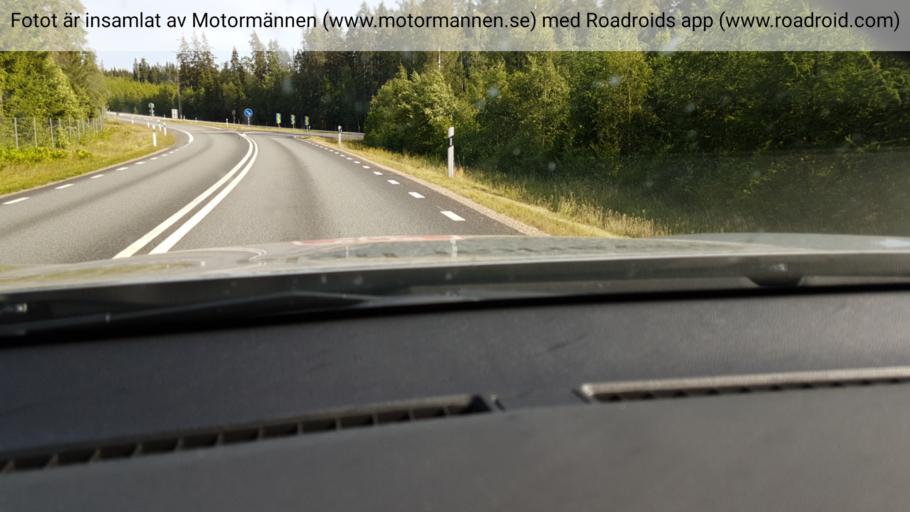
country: SE
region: Joenkoeping
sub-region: Vetlanda Kommun
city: Ekenassjon
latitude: 57.5147
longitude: 14.9882
